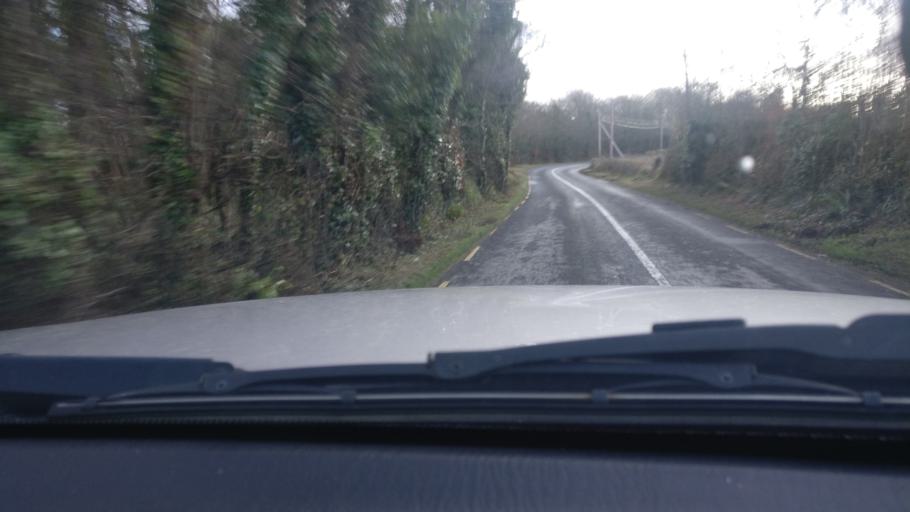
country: IE
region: Connaught
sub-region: County Galway
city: Ballinasloe
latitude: 53.2807
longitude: -8.2418
